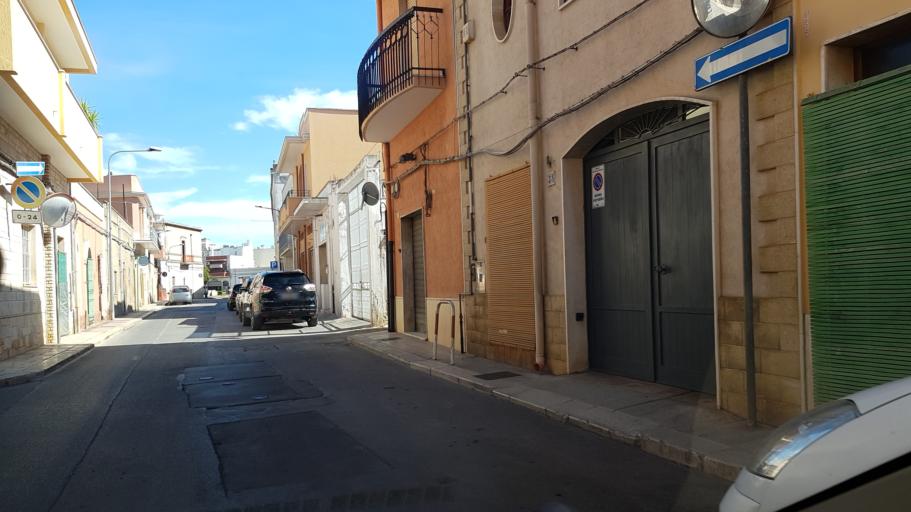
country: IT
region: Apulia
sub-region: Provincia di Brindisi
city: San Vito dei Normanni
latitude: 40.6593
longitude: 17.7011
